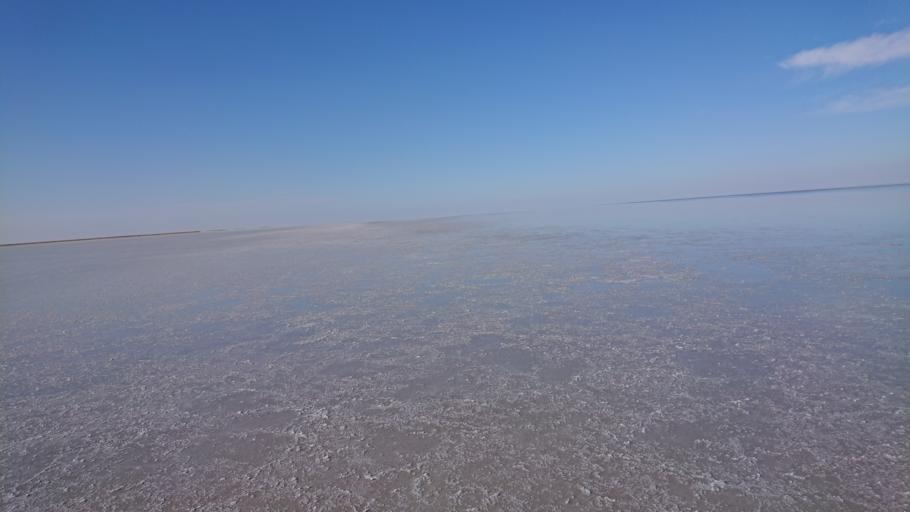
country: TR
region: Aksaray
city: Eskil
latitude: 38.4934
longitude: 33.4823
